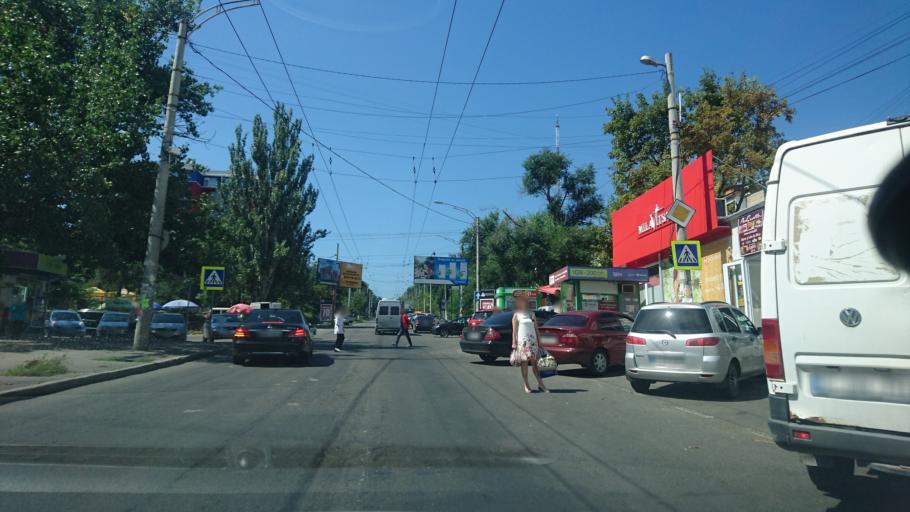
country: MD
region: Chisinau
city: Chisinau
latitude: 47.0023
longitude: 28.8159
